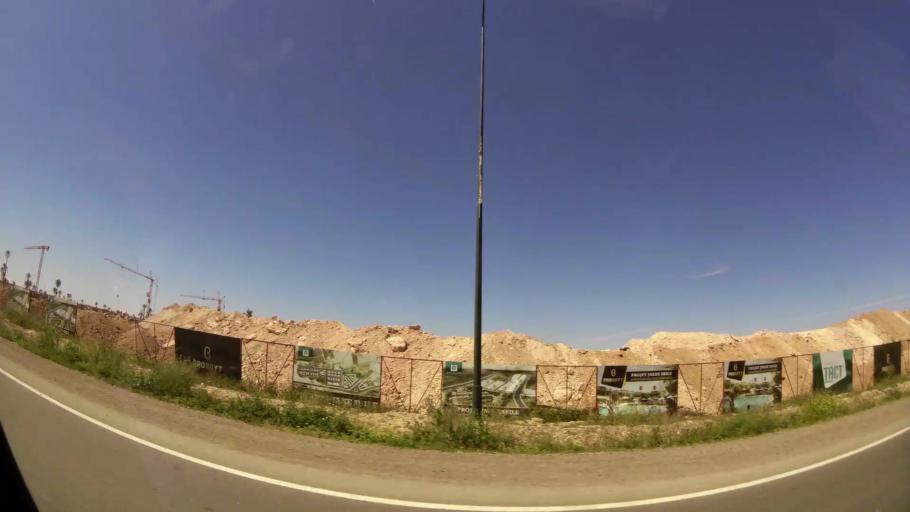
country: MA
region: Marrakech-Tensift-Al Haouz
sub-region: Marrakech
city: Marrakesh
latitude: 31.6758
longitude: -7.9913
